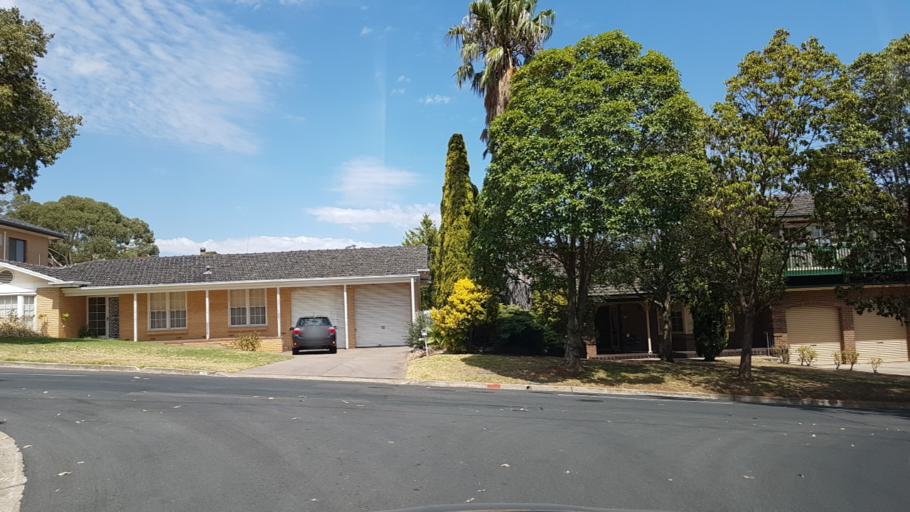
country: AU
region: South Australia
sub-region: Burnside
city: Hazelwood Park
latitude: -34.9398
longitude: 138.6645
